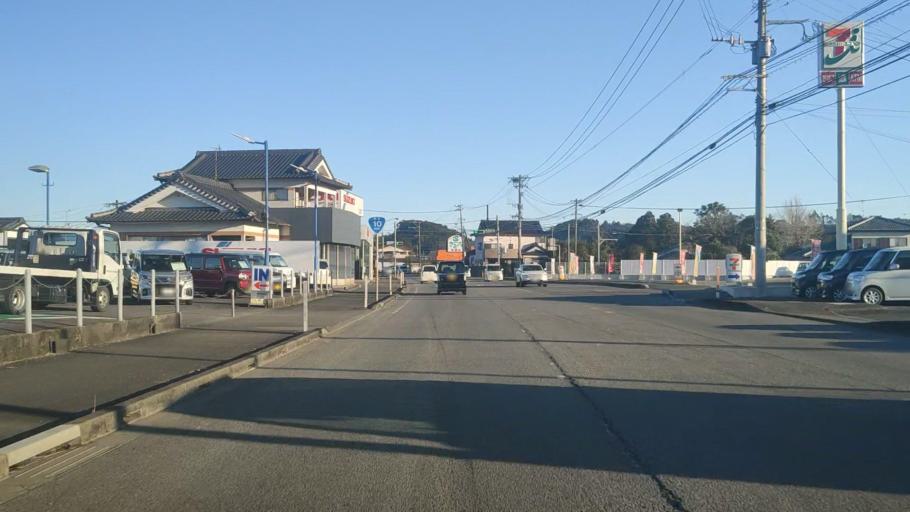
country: JP
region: Miyazaki
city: Takanabe
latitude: 32.1371
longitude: 131.5274
